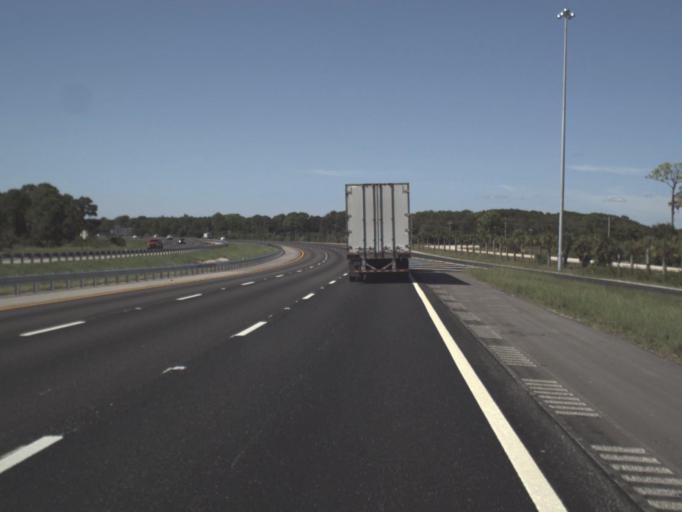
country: US
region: Florida
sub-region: Lee County
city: Tice
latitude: 26.7175
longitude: -81.8134
